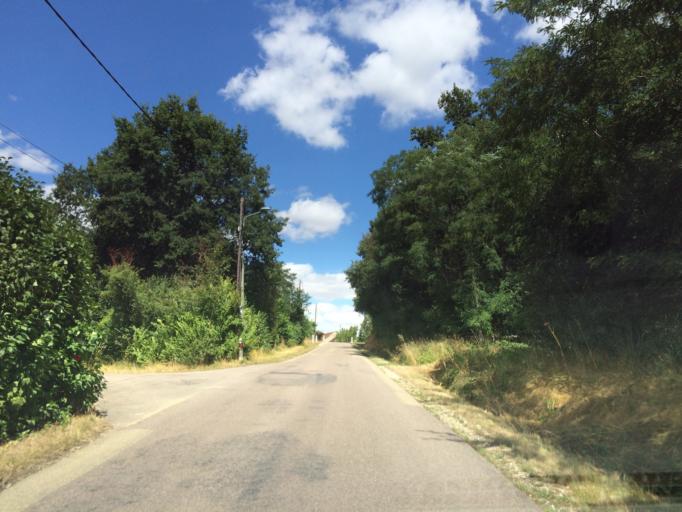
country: FR
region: Bourgogne
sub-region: Departement de l'Yonne
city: Fleury-la-Vallee
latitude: 47.8678
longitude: 3.4054
